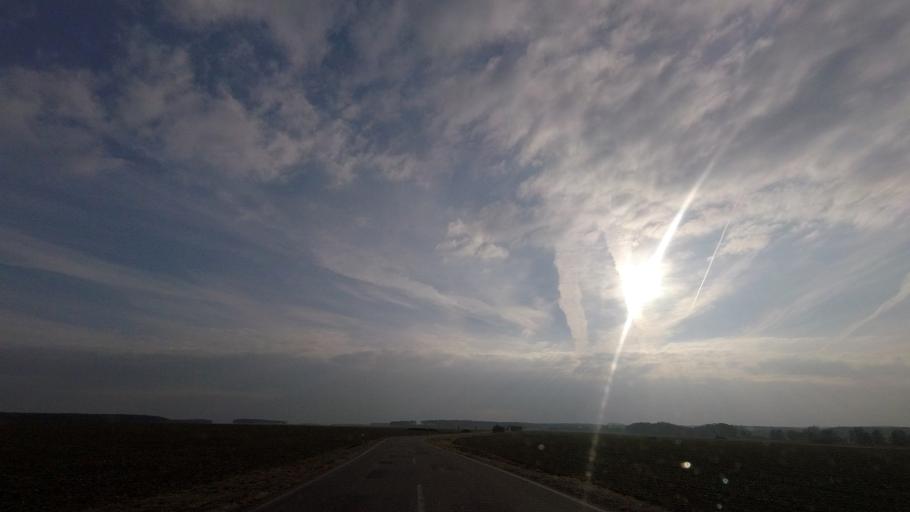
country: DE
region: Brandenburg
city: Belzig
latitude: 52.1470
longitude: 12.6557
